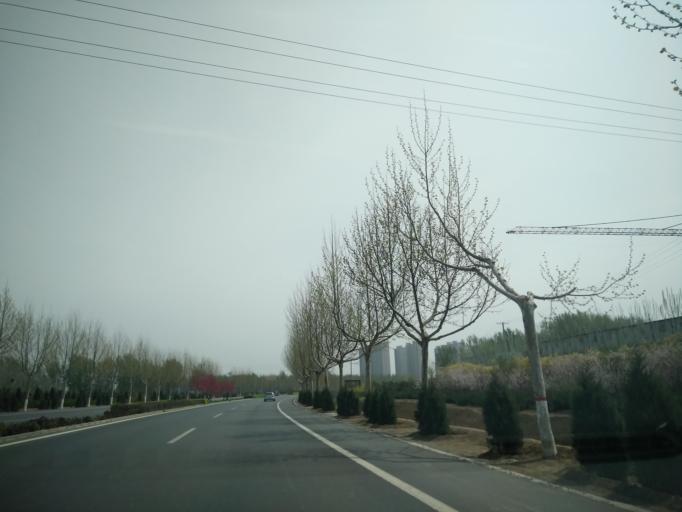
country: CN
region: Beijing
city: Xiji
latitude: 39.7930
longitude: 116.9392
